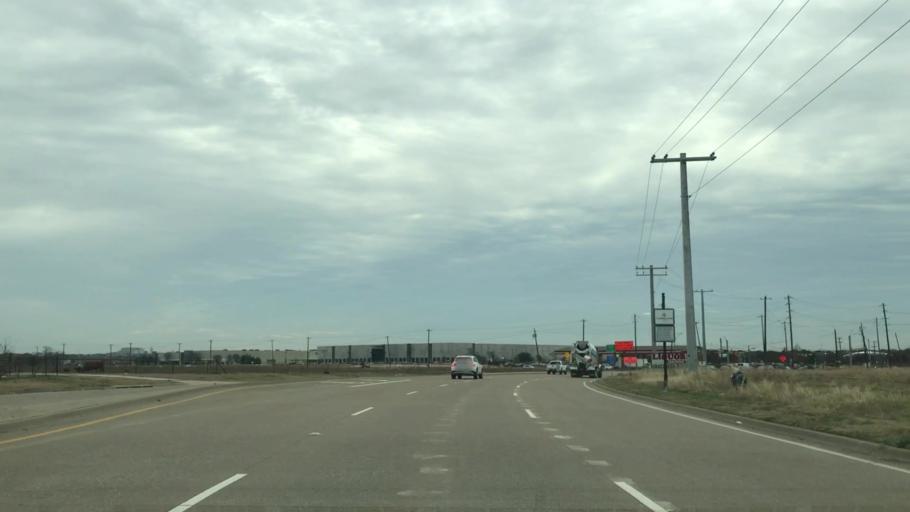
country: US
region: Texas
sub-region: Denton County
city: The Colony
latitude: 33.0469
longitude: -96.8821
